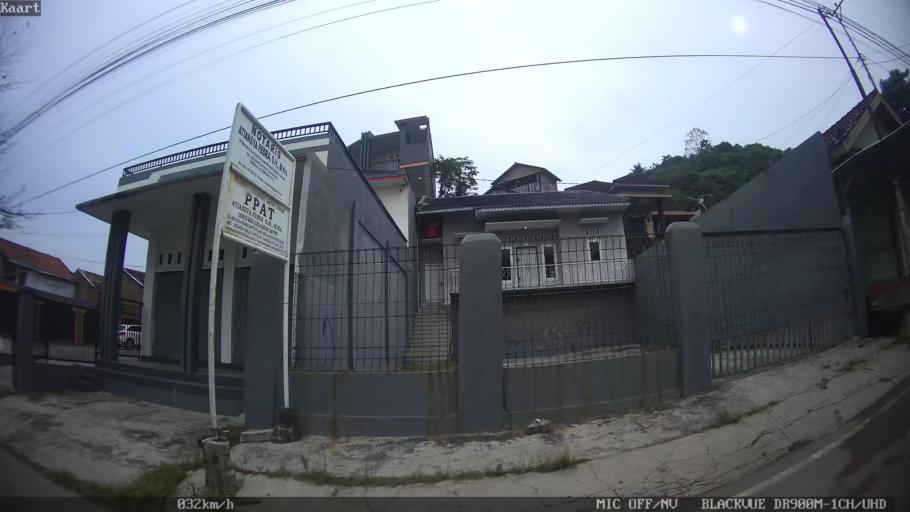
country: ID
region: Lampung
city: Bandarlampung
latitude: -5.4081
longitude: 105.2433
